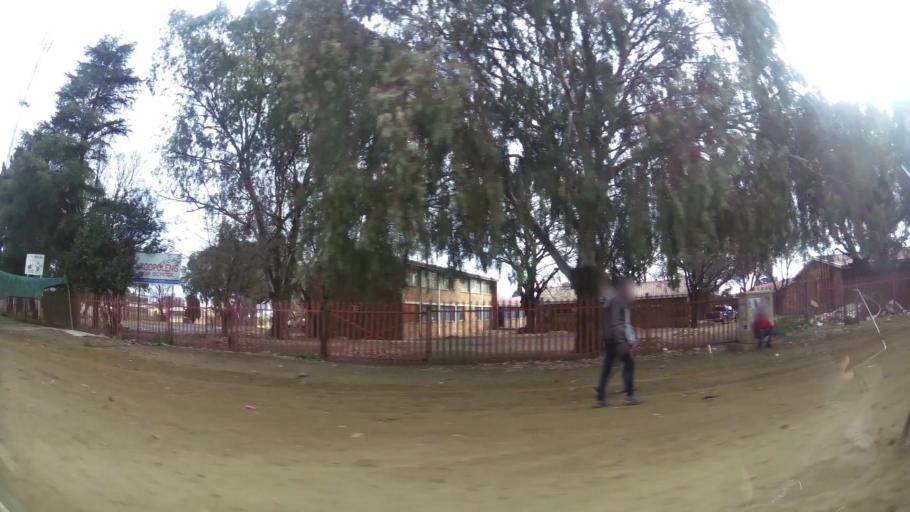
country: ZA
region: Orange Free State
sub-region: Fezile Dabi District Municipality
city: Sasolburg
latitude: -26.8436
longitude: 27.8461
